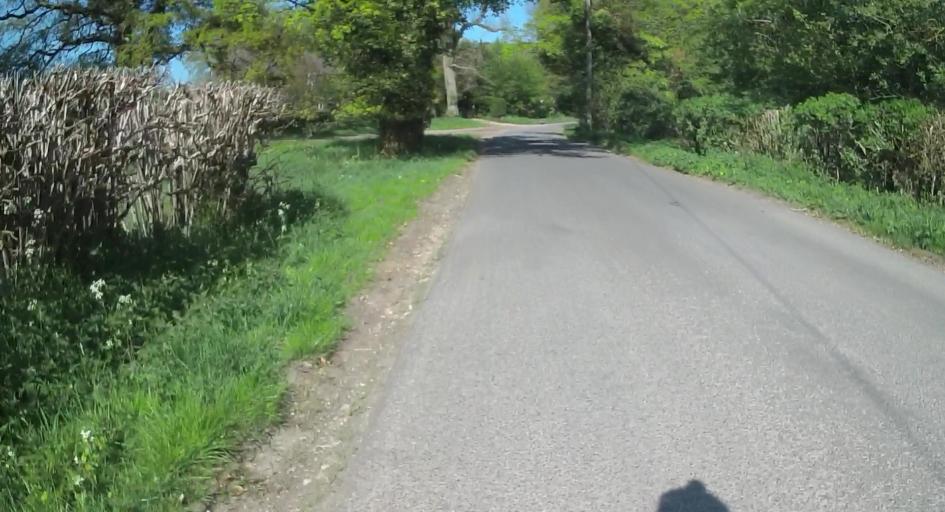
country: GB
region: England
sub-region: Hampshire
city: Alton
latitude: 51.1639
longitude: -1.0238
